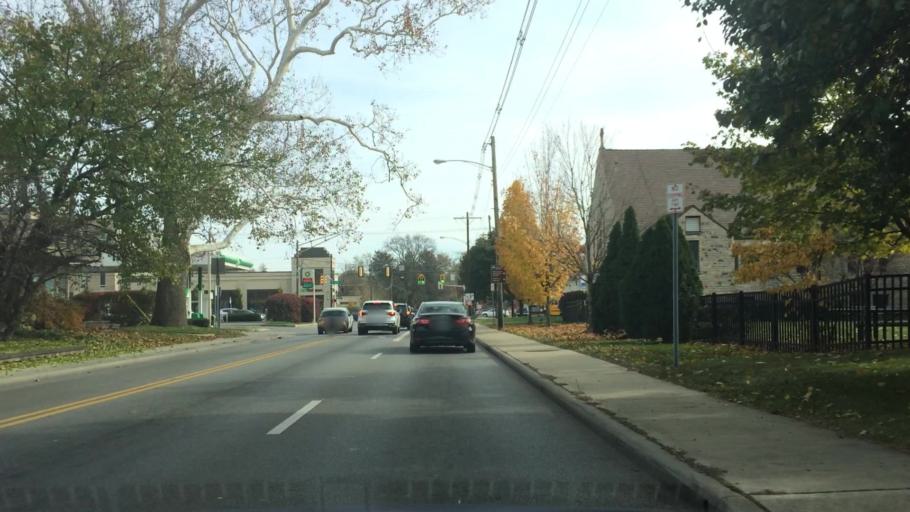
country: US
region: Ohio
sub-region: Franklin County
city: Worthington
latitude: 40.0515
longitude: -83.0215
